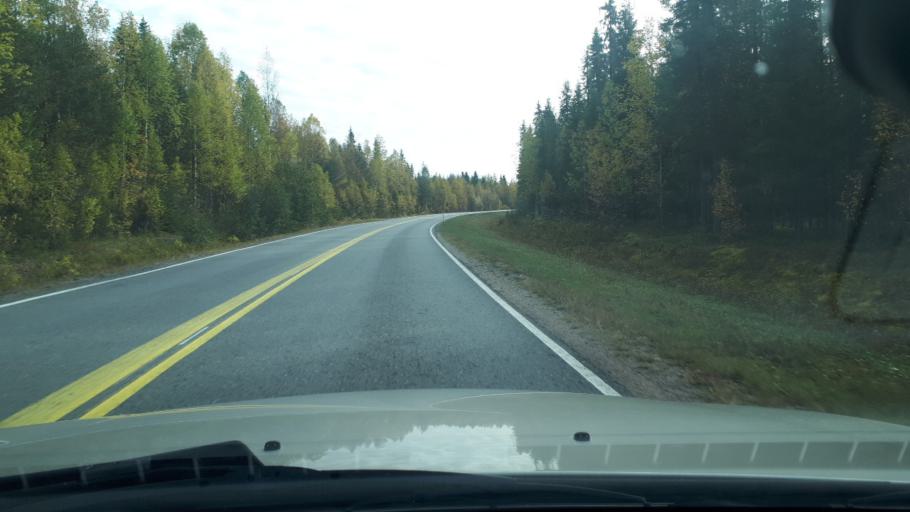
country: FI
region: Lapland
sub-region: Rovaniemi
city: Ranua
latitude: 65.9680
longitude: 26.0137
